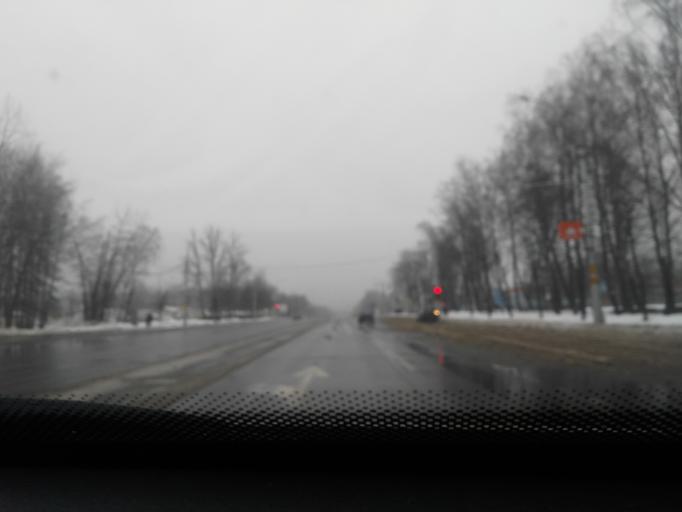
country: BY
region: Mogilev
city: Babruysk
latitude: 53.1724
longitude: 29.2029
